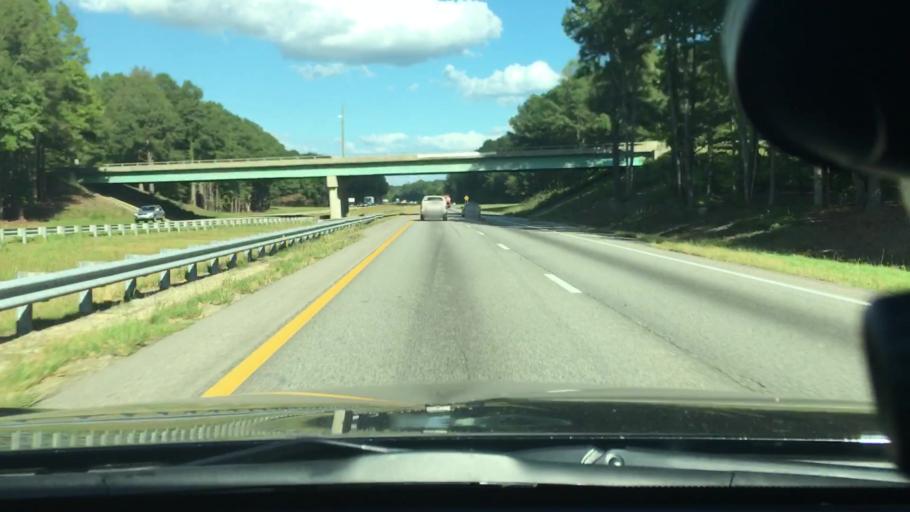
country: US
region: North Carolina
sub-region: Wake County
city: Wendell
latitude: 35.8242
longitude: -78.3756
